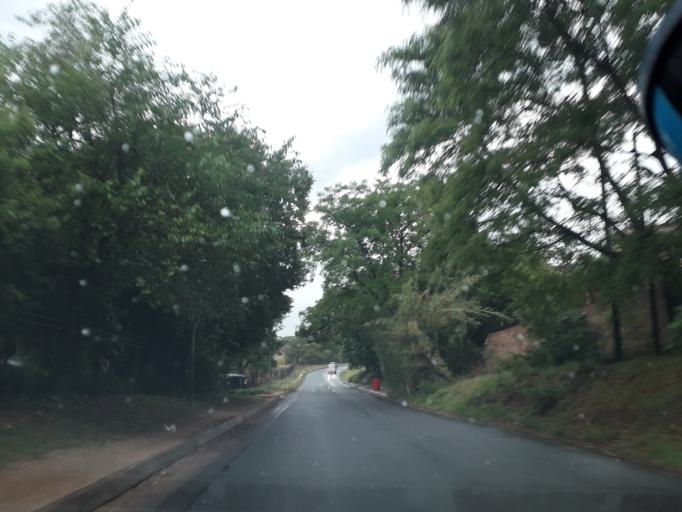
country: ZA
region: Gauteng
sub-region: City of Johannesburg Metropolitan Municipality
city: Johannesburg
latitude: -26.0784
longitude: 27.9857
